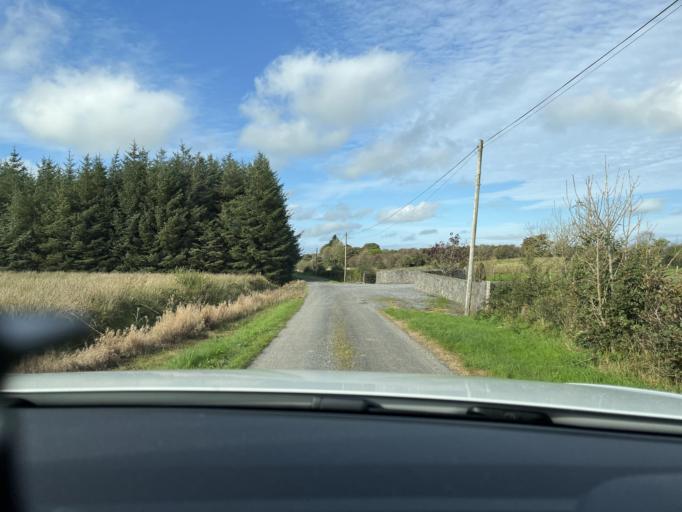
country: IE
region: Connaught
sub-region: Sligo
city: Ballymote
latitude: 54.0687
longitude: -8.4246
